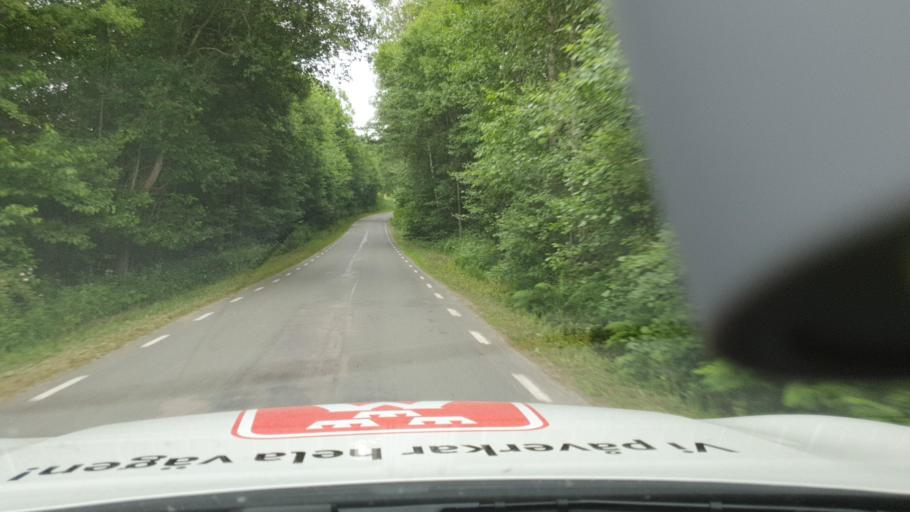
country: SE
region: Vaestra Goetaland
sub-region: Hjo Kommun
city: Hjo
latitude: 58.1762
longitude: 14.1886
